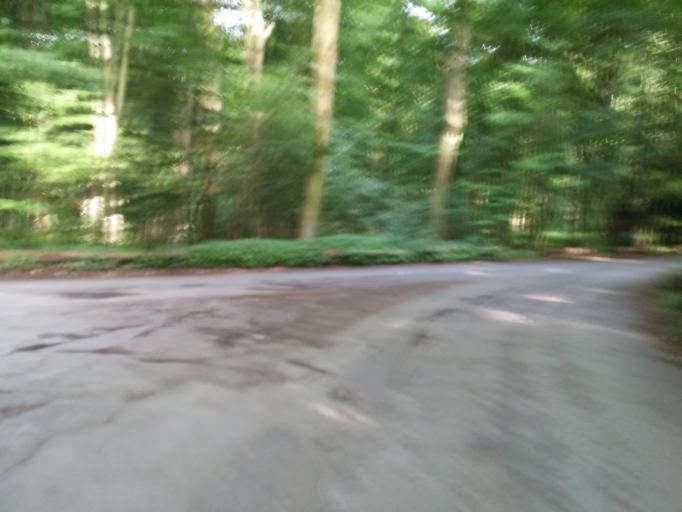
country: DE
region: North Rhine-Westphalia
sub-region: Regierungsbezirk Dusseldorf
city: Krefeld
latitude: 51.3887
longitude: 6.5381
